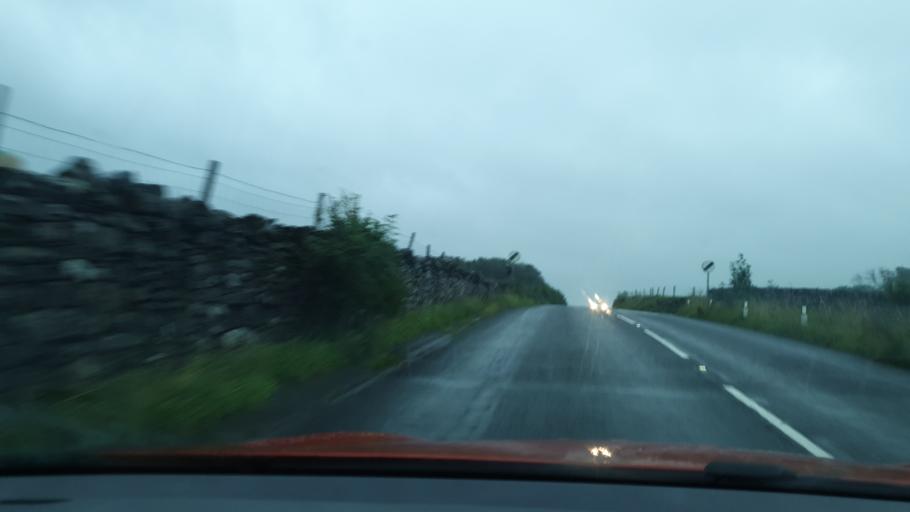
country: GB
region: England
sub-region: Cumbria
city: Ulverston
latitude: 54.2546
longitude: -3.0727
